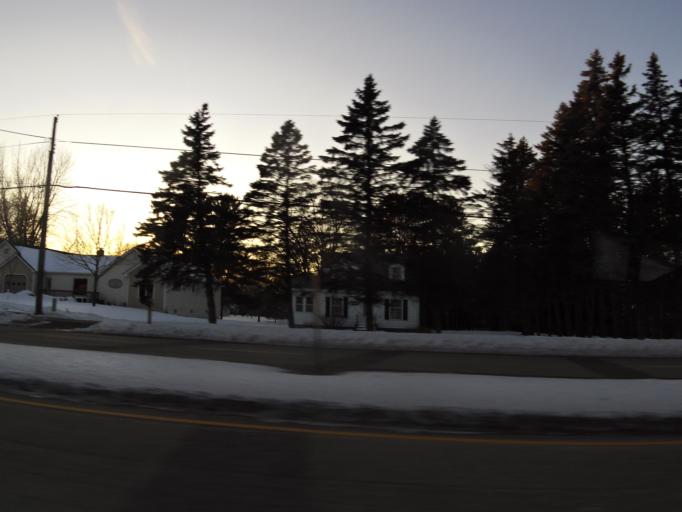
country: US
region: Minnesota
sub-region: Ramsey County
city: North Saint Paul
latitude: 45.0439
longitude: -93.0153
